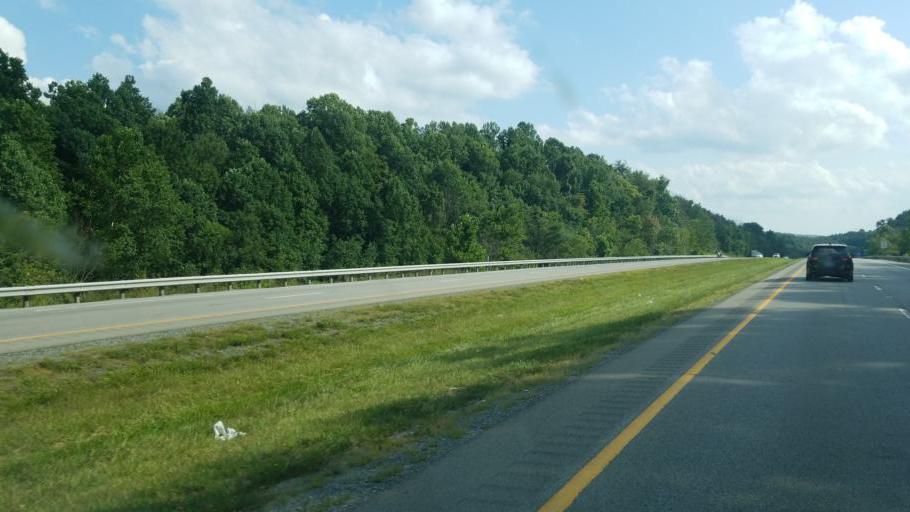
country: US
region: West Virginia
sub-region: Monongalia County
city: Brookhaven
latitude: 39.6352
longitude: -79.8993
